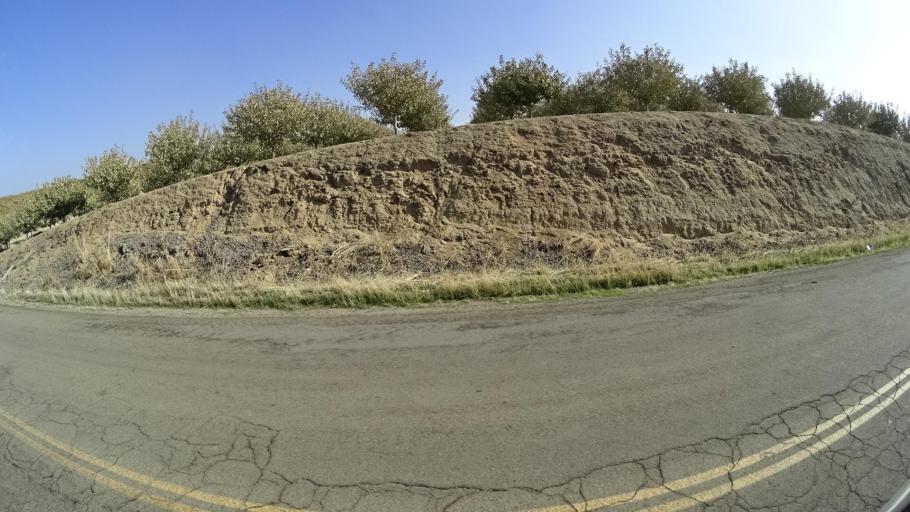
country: US
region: California
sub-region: Kern County
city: McFarland
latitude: 35.6452
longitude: -119.1336
